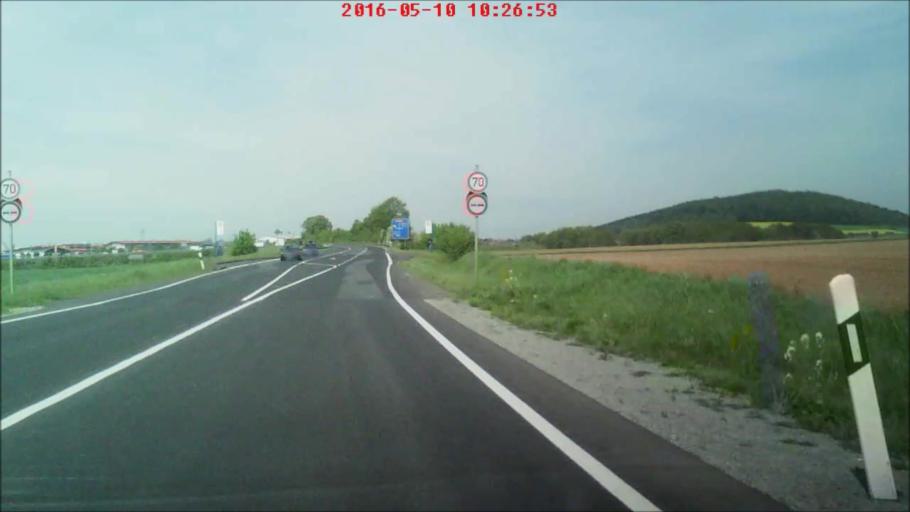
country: DE
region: Hesse
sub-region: Regierungsbezirk Kassel
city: Kunzell
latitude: 50.5527
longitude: 9.7405
